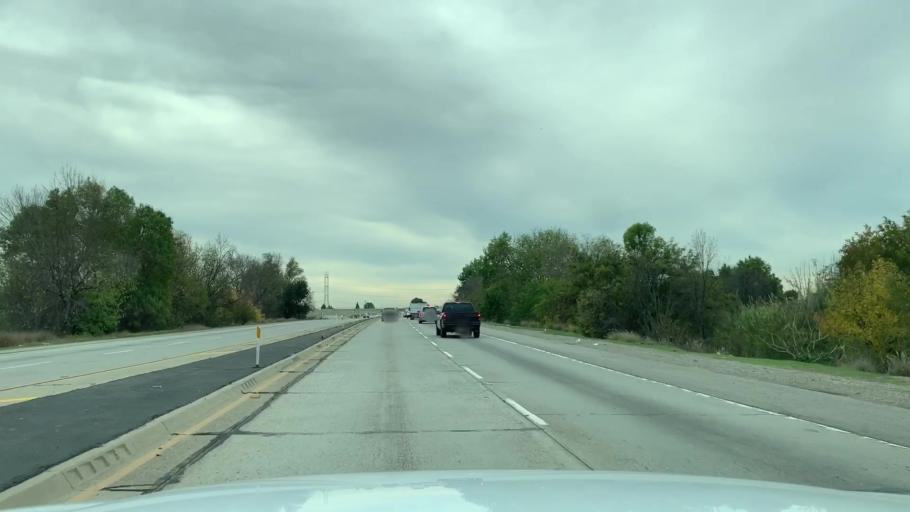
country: US
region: California
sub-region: Los Angeles County
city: South El Monte
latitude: 34.0262
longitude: -118.0695
